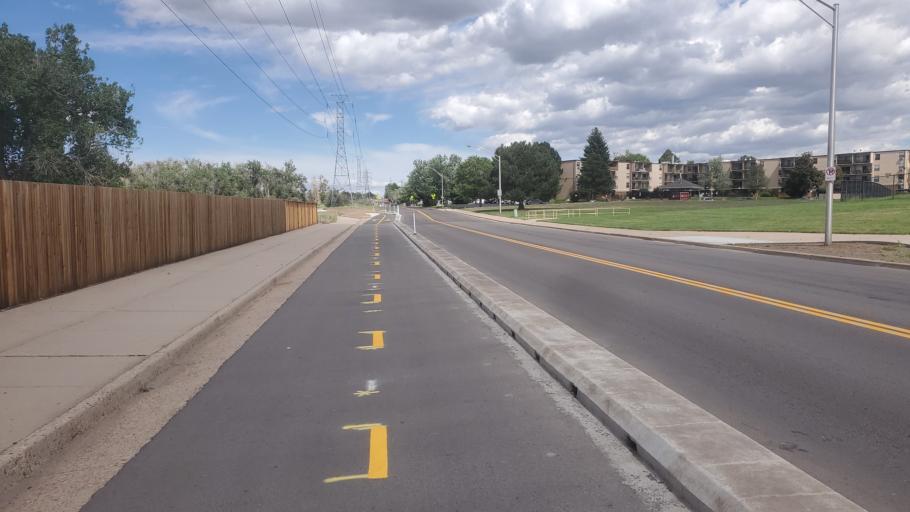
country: US
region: Colorado
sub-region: Adams County
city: Aurora
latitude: 39.6821
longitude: -104.8393
